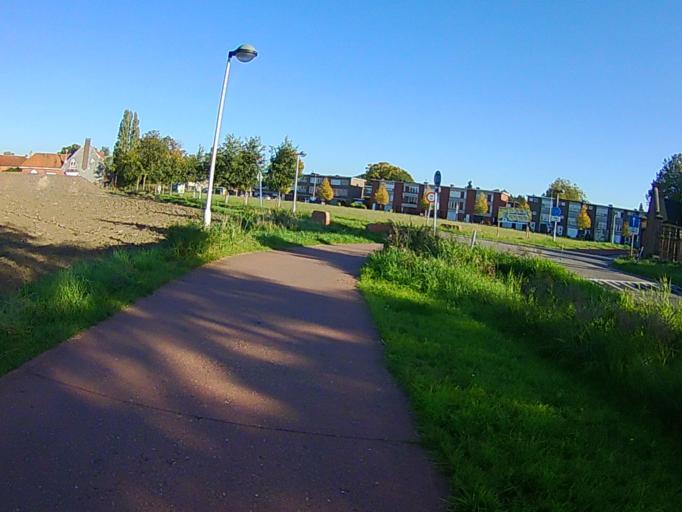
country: BE
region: Flanders
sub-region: Provincie Antwerpen
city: Kapellen
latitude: 51.2883
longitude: 4.4272
